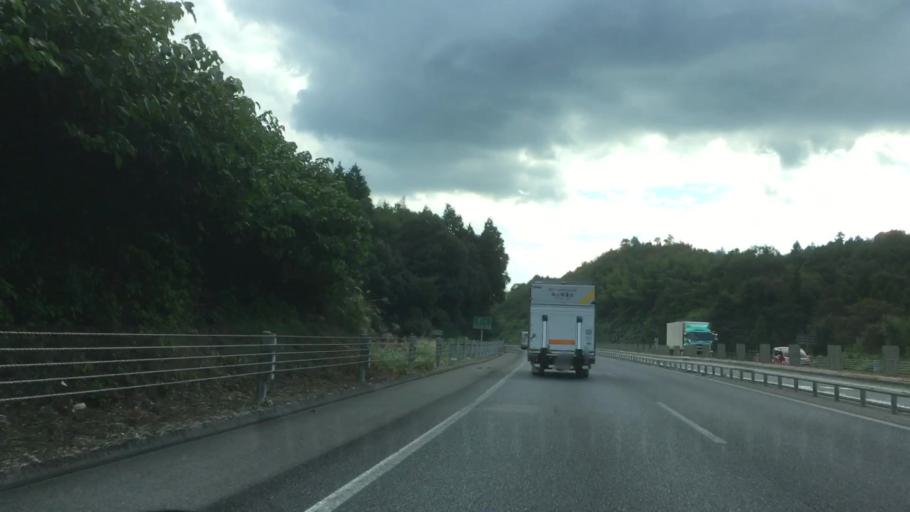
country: JP
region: Yamaguchi
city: Iwakuni
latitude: 34.1333
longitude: 132.1141
